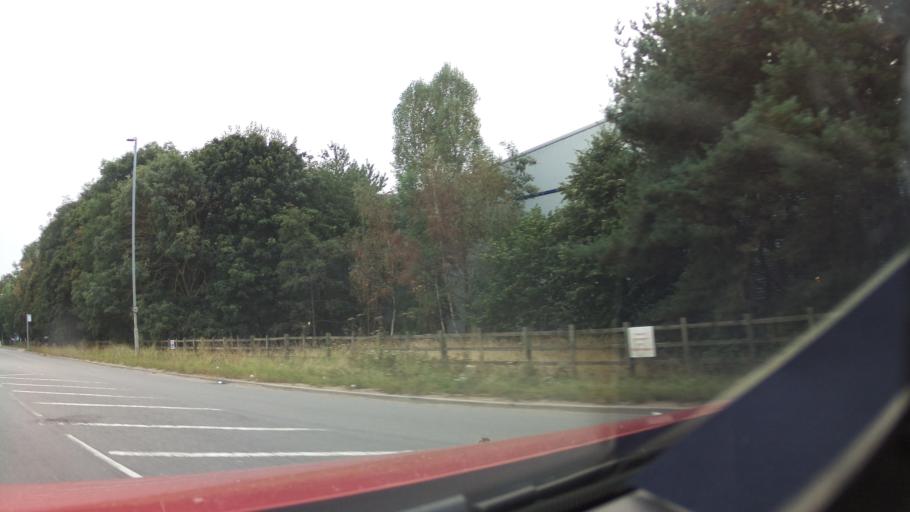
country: GB
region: England
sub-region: Nottinghamshire
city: South Collingham
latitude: 53.1515
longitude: -0.6704
